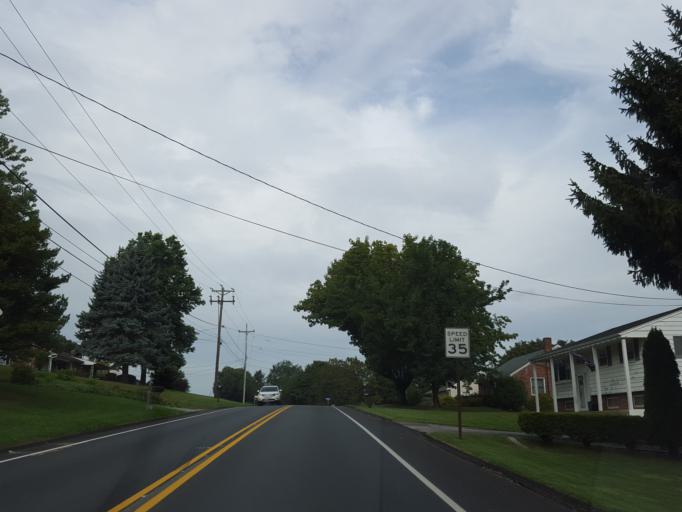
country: US
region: Pennsylvania
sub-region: York County
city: Spry
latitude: 39.9096
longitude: -76.6925
